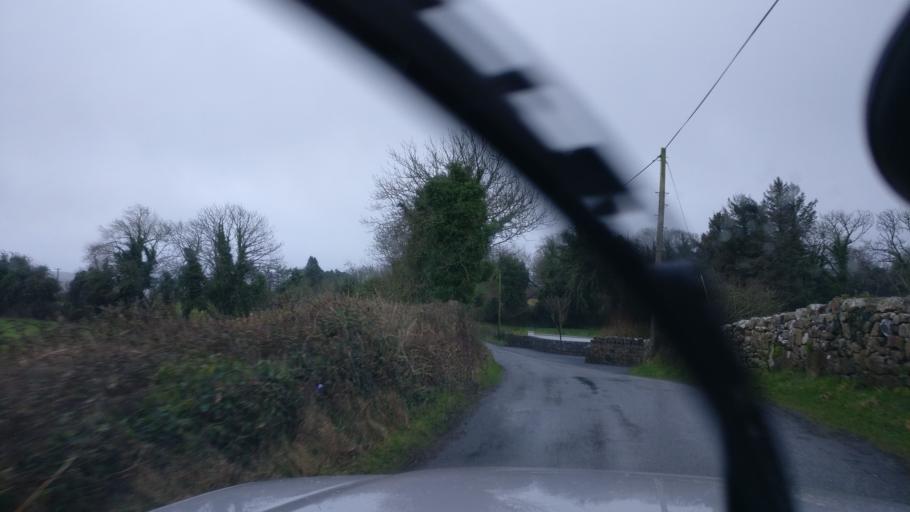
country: IE
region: Connaught
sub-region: County Galway
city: Loughrea
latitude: 53.1701
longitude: -8.6461
